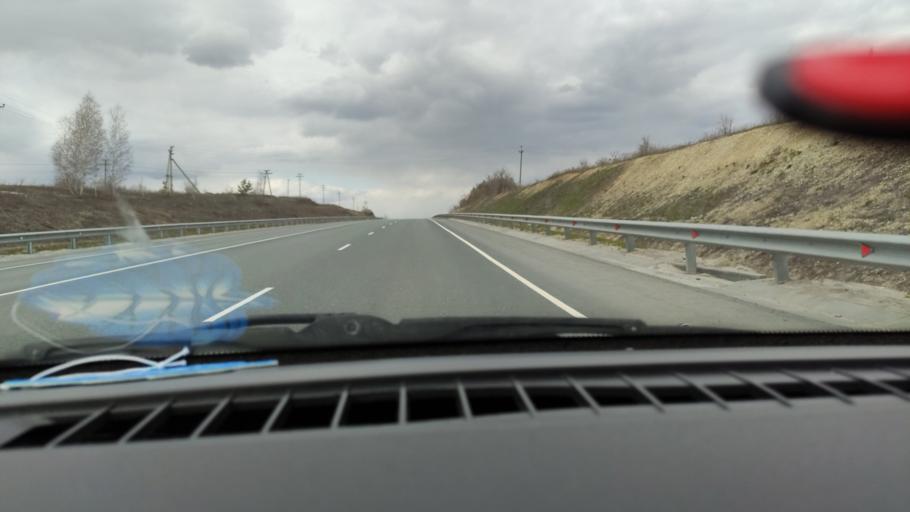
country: RU
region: Saratov
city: Shikhany
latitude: 52.1463
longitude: 47.1966
